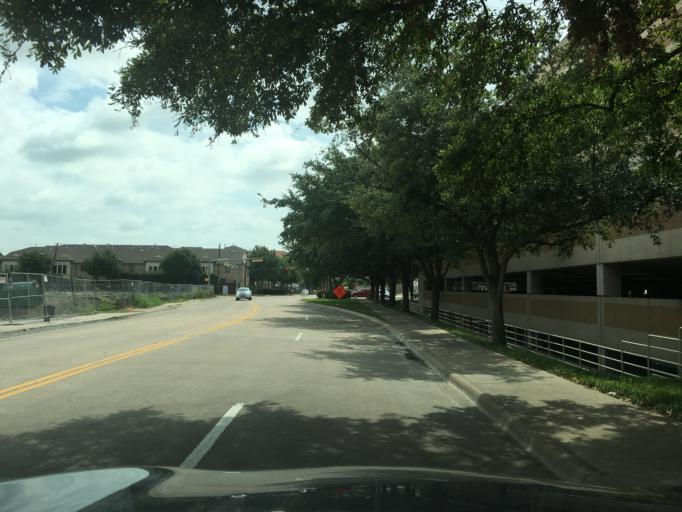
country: US
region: Texas
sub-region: Dallas County
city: Addison
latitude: 32.9360
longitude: -96.8201
